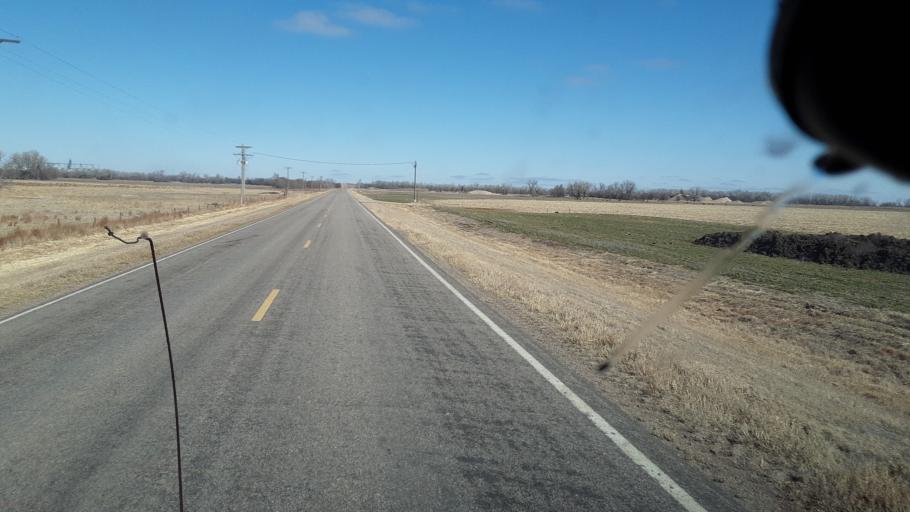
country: US
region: Kansas
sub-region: Barton County
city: Ellinwood
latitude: 38.3422
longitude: -98.6642
